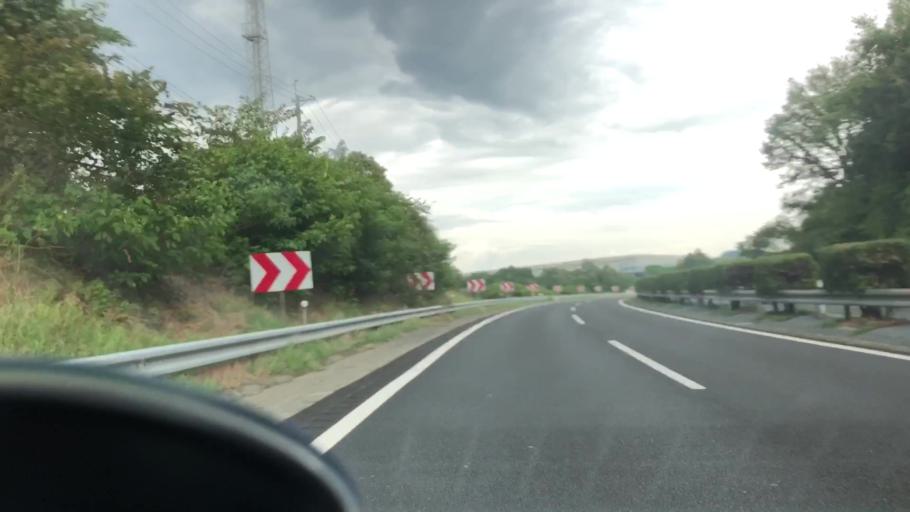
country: JP
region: Hyogo
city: Yashiro
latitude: 34.9389
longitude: 134.8723
